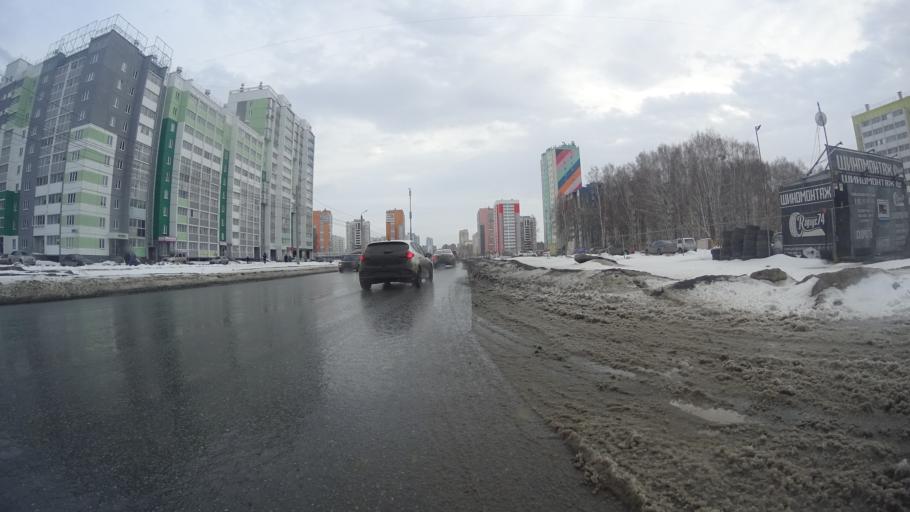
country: RU
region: Chelyabinsk
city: Roshchino
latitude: 55.2129
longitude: 61.2842
